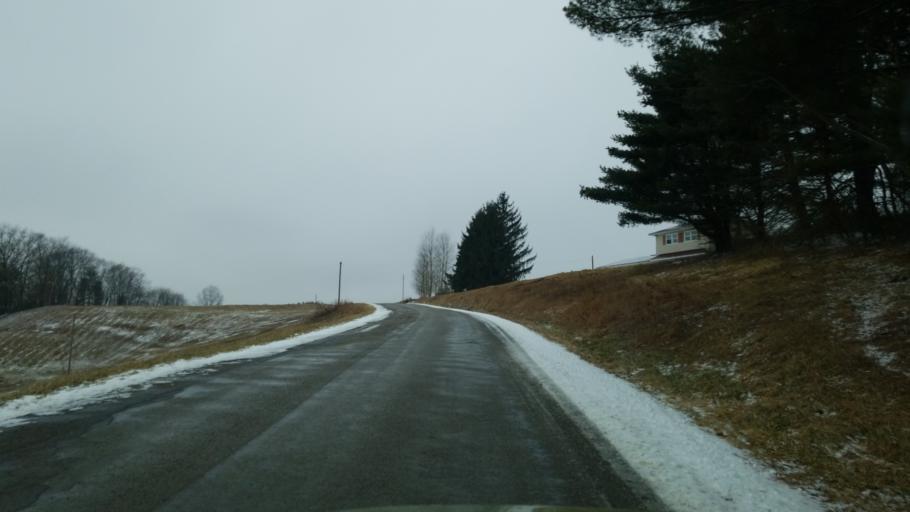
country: US
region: Pennsylvania
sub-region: Jefferson County
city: Sykesville
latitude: 41.0837
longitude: -78.8194
